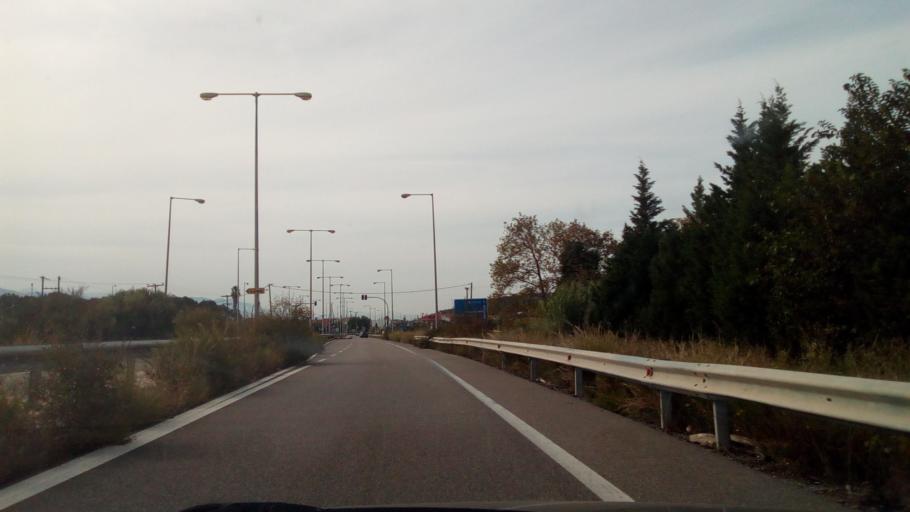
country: GR
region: West Greece
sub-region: Nomos Aitolias kai Akarnanias
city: Antirrio
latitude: 38.3716
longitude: 21.7812
